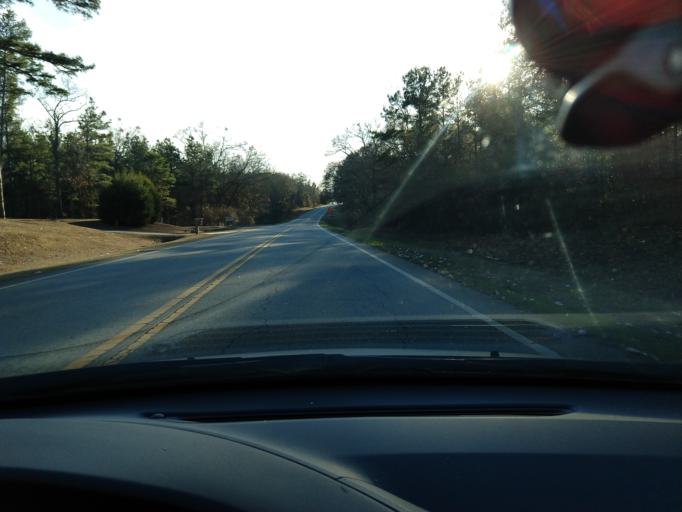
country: US
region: Georgia
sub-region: Sumter County
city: Americus
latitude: 32.1264
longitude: -84.1546
